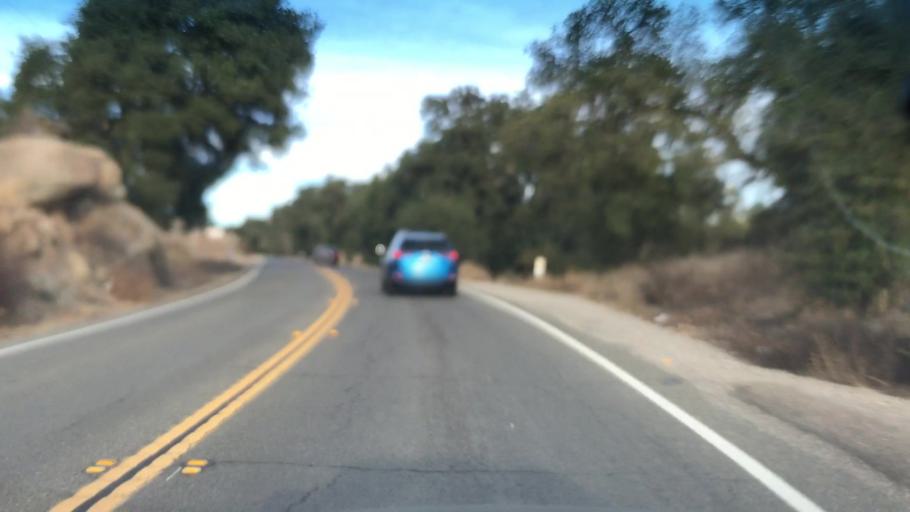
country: US
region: California
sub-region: San Diego County
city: Ramona
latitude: 33.0562
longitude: -116.8191
